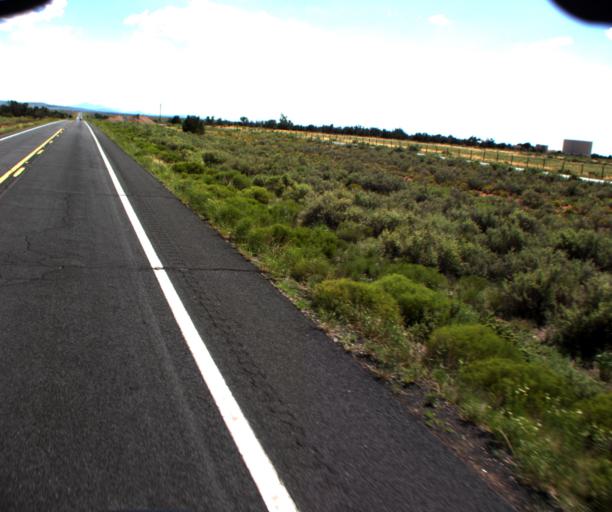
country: US
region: Arizona
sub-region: Coconino County
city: Williams
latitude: 35.6463
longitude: -112.1403
